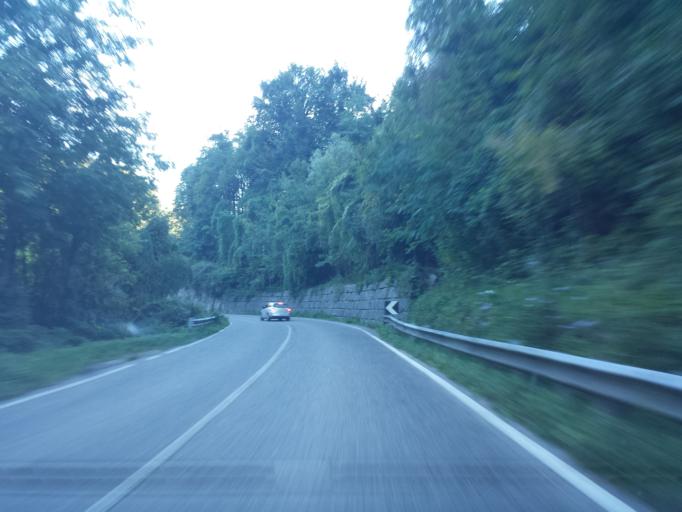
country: IT
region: Veneto
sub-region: Provincia di Vicenza
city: San Quirico
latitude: 45.6906
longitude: 11.2602
